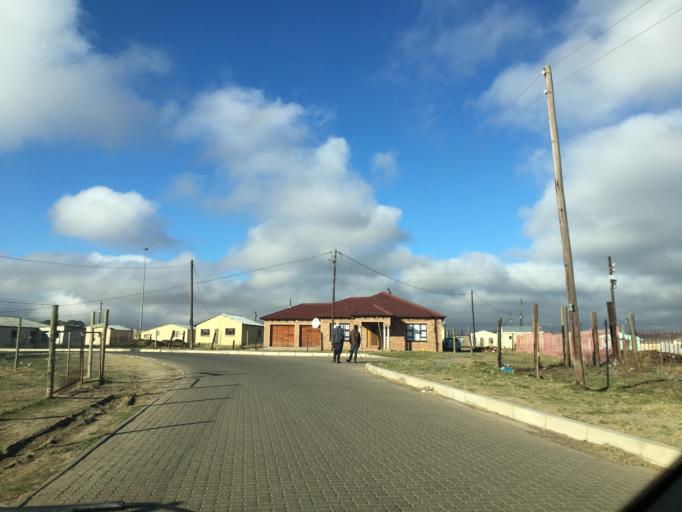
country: ZA
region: Eastern Cape
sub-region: Chris Hani District Municipality
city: Elliot
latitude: -31.3360
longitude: 27.8354
